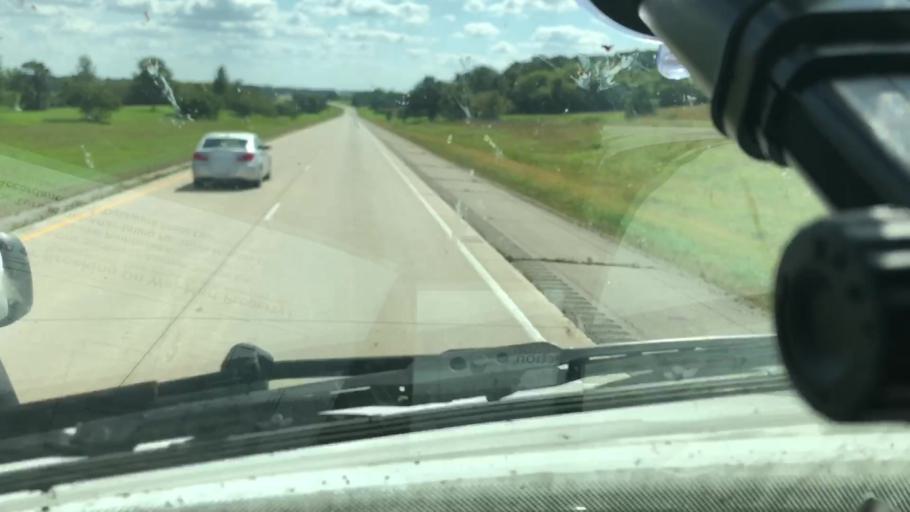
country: US
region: Minnesota
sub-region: Freeborn County
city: Albert Lea
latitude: 43.5167
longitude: -93.3553
